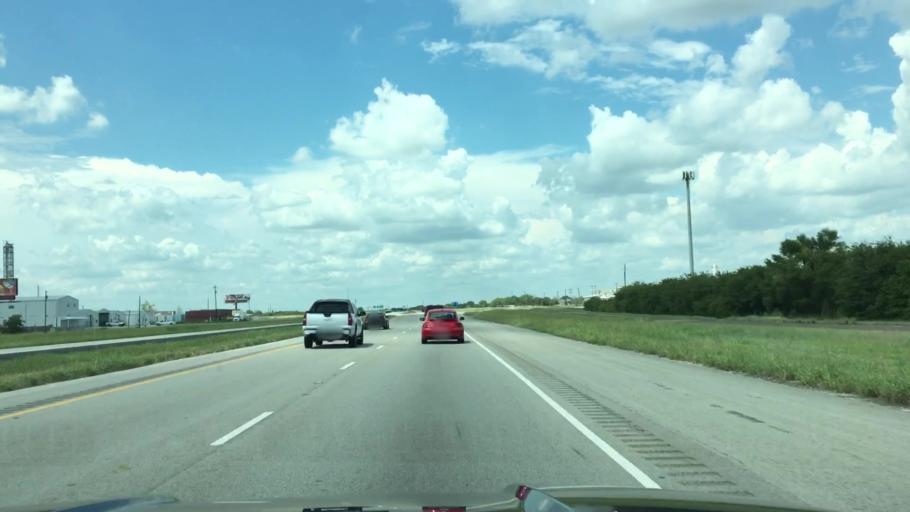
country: US
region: Texas
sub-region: Wise County
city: Rhome
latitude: 33.0334
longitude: -97.4501
